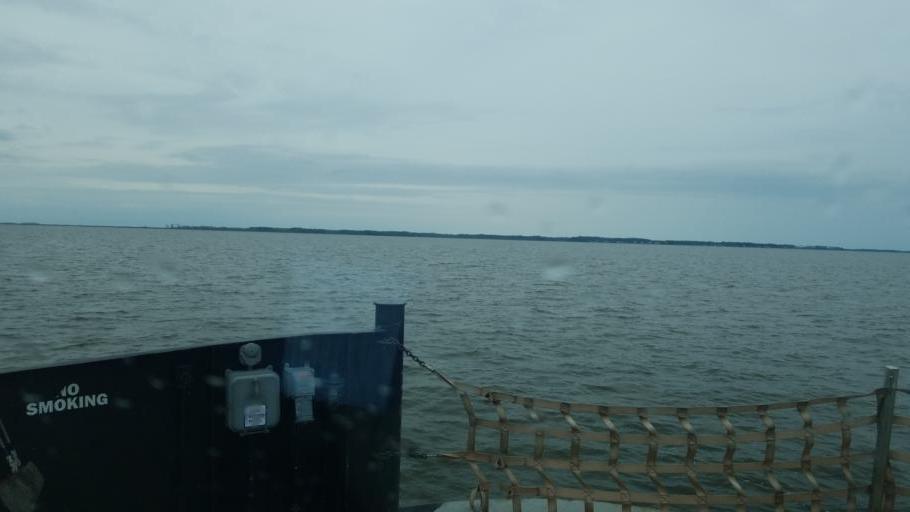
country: US
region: North Carolina
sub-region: Currituck County
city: Currituck
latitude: 36.4658
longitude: -75.9640
